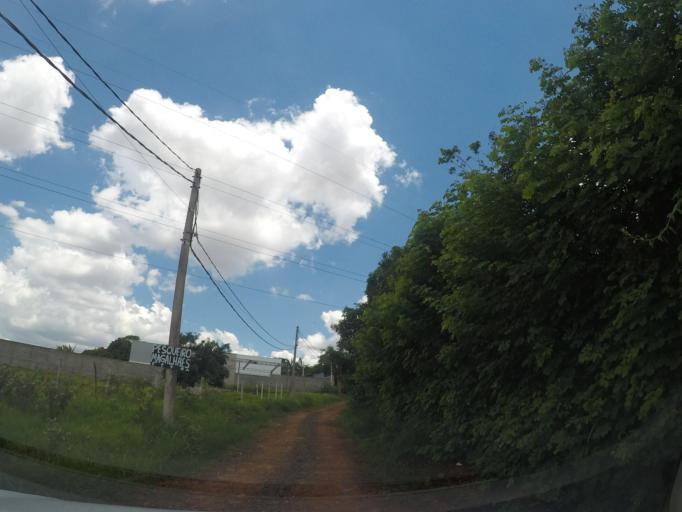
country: BR
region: Sao Paulo
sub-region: Hortolandia
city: Hortolandia
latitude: -22.8374
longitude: -47.2398
